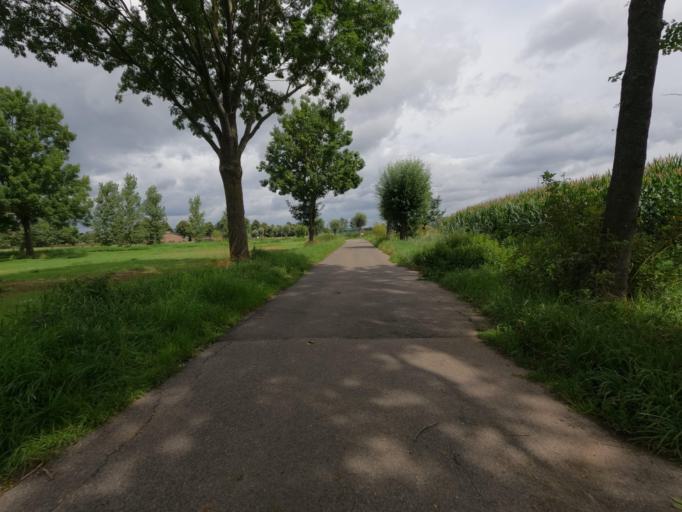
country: DE
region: North Rhine-Westphalia
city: Huckelhoven
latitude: 51.0252
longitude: 6.1803
